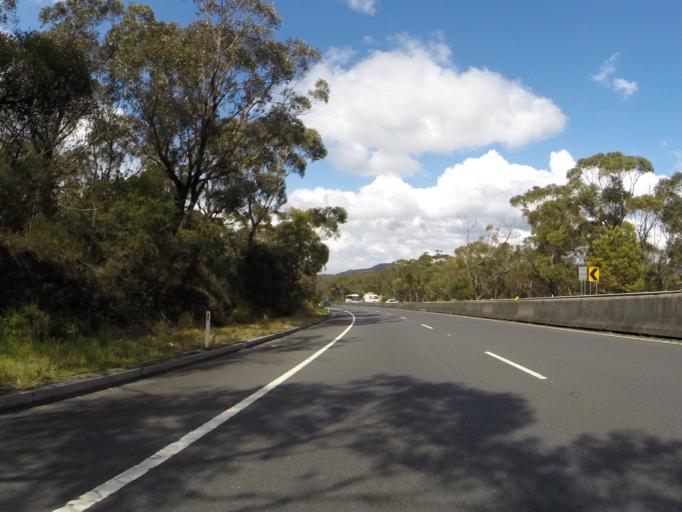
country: AU
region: New South Wales
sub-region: Wollongong
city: Mount Ousley
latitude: -34.3577
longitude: 150.8573
